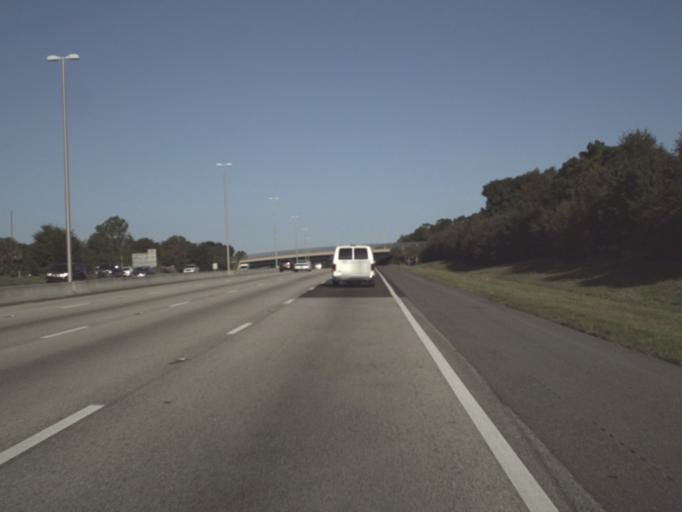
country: US
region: Florida
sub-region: Orange County
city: Gotha
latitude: 28.5255
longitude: -81.5136
